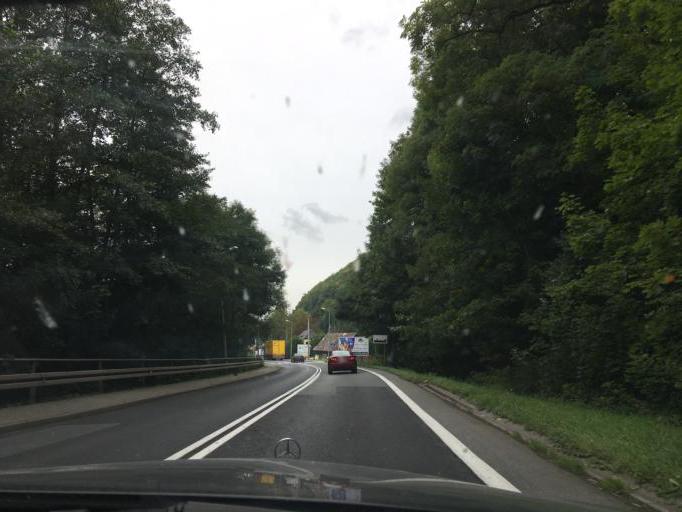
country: PL
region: Lower Silesian Voivodeship
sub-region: Powiat klodzki
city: Lewin Klodzki
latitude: 50.4090
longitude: 16.2749
